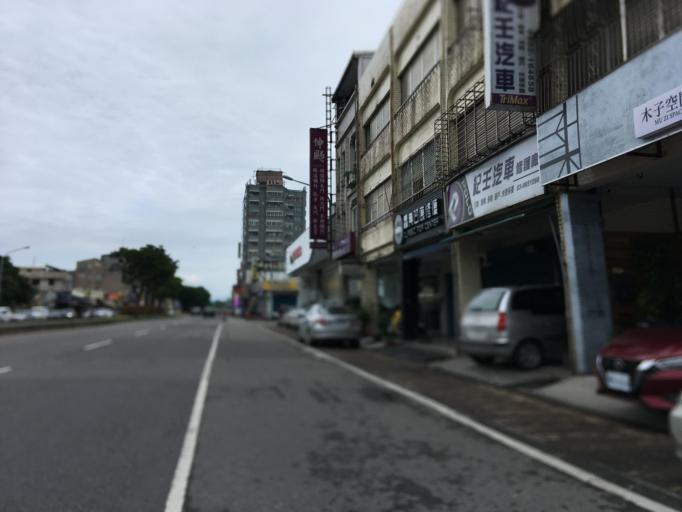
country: TW
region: Taiwan
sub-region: Yilan
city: Yilan
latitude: 24.7058
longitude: 121.7712
